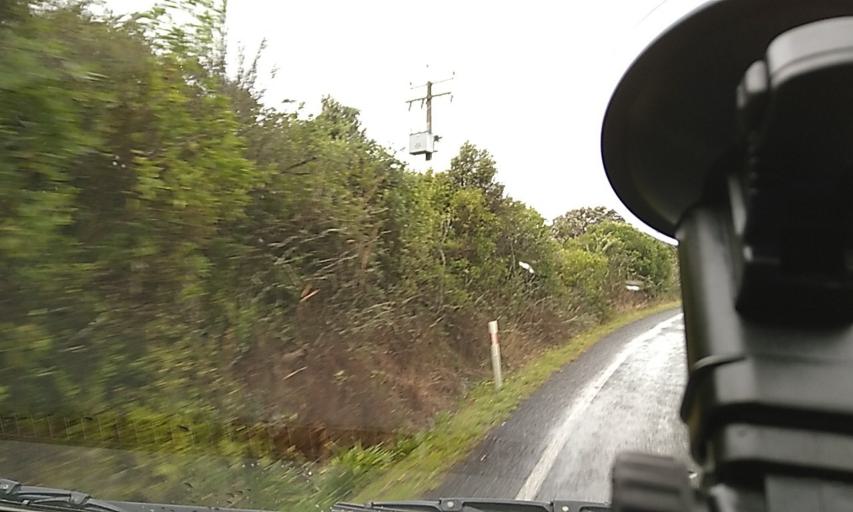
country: NZ
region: Auckland
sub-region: Auckland
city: Pukekohe East
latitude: -37.3072
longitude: 174.9364
